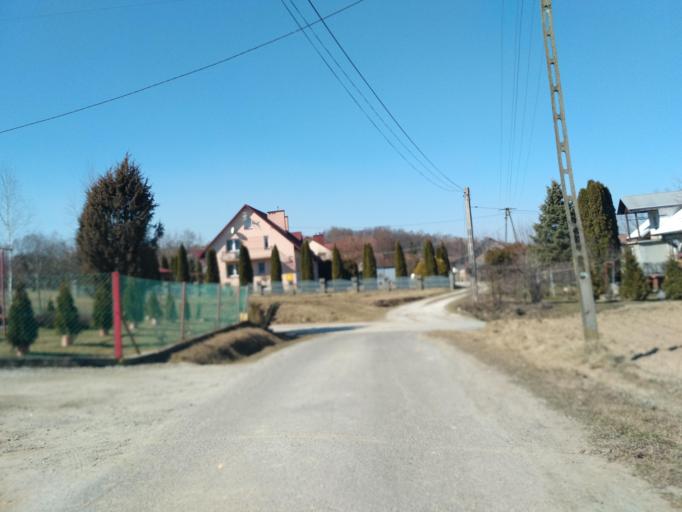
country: PL
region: Subcarpathian Voivodeship
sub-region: Powiat ropczycko-sedziszowski
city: Wielopole Skrzynskie
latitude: 49.9568
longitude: 21.5815
